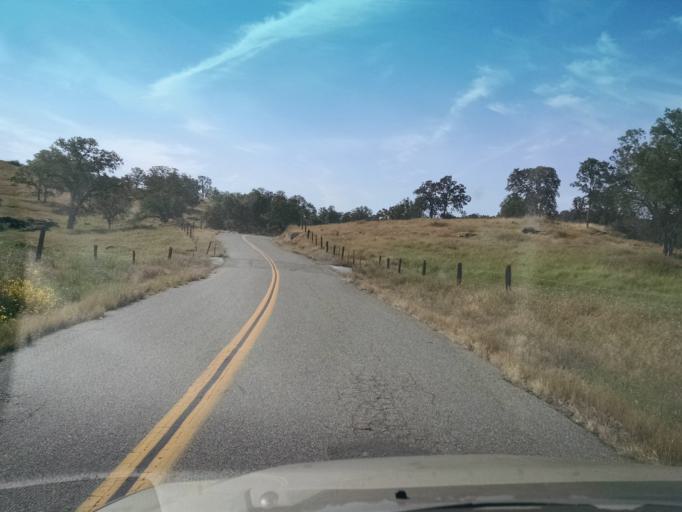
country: US
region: California
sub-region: Madera County
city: Yosemite Lakes
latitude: 37.1119
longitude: -119.6948
